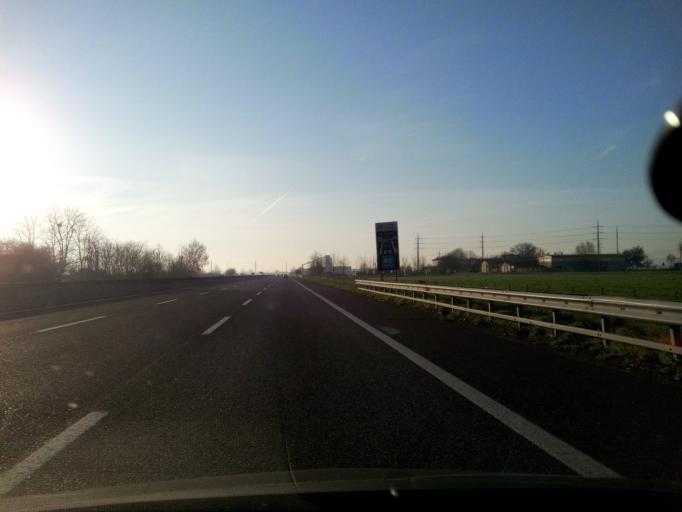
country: IT
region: Lombardy
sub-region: Provincia di Lodi
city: Somaglia
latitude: 45.1361
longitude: 9.6457
